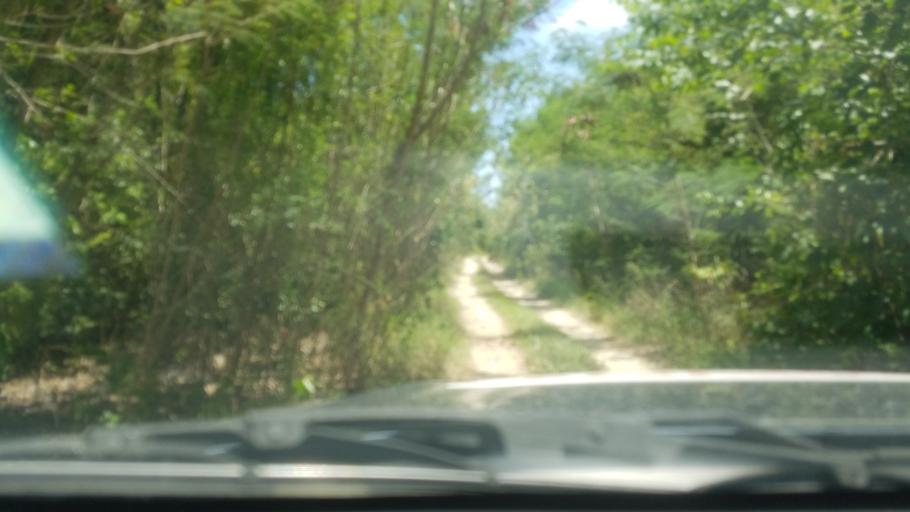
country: LC
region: Vieux-Fort
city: Vieux Fort
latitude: 13.7499
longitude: -60.9370
